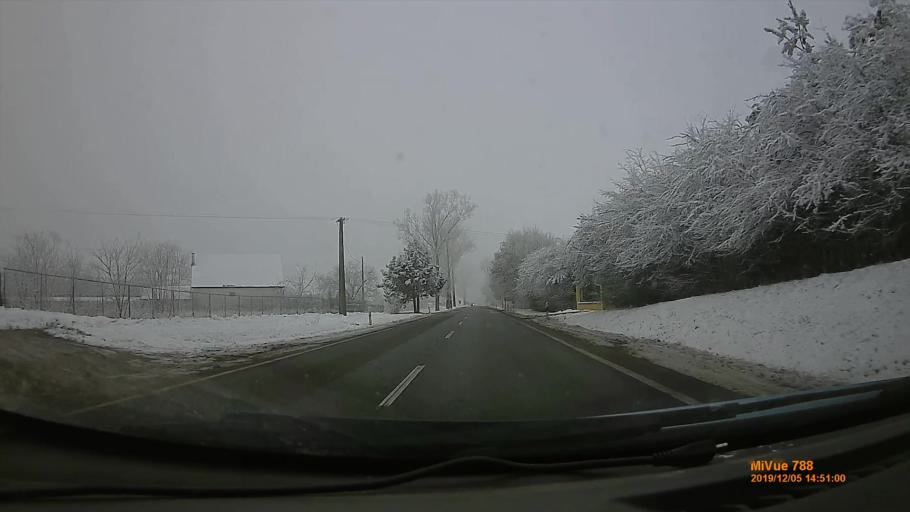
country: HU
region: Szabolcs-Szatmar-Bereg
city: Nyirtelek
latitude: 47.9904
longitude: 21.6639
